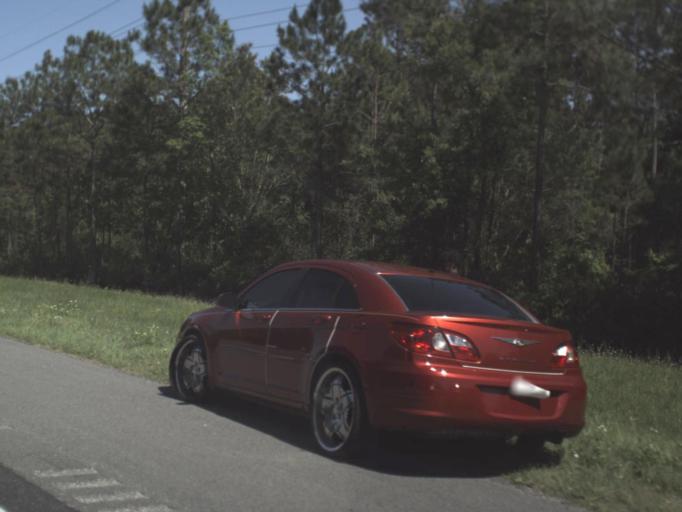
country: US
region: Florida
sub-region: Duval County
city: Baldwin
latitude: 30.2904
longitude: -81.9622
